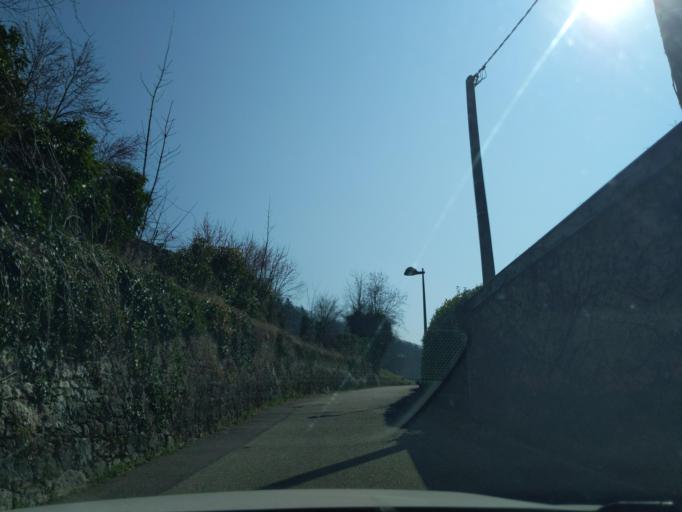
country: FR
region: Rhone-Alpes
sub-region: Departement de la Savoie
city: Chindrieux
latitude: 45.8861
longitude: 5.8453
